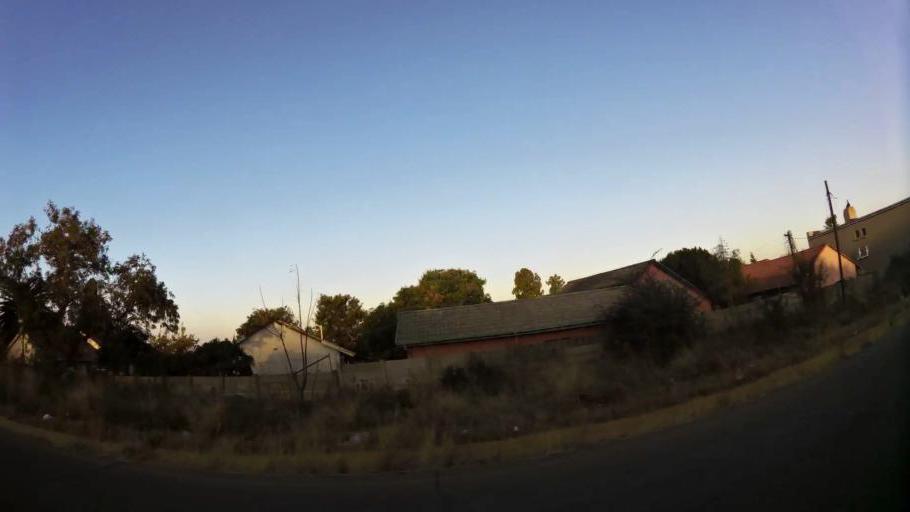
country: ZA
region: North-West
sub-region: Bojanala Platinum District Municipality
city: Rustenburg
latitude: -25.6366
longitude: 27.2010
